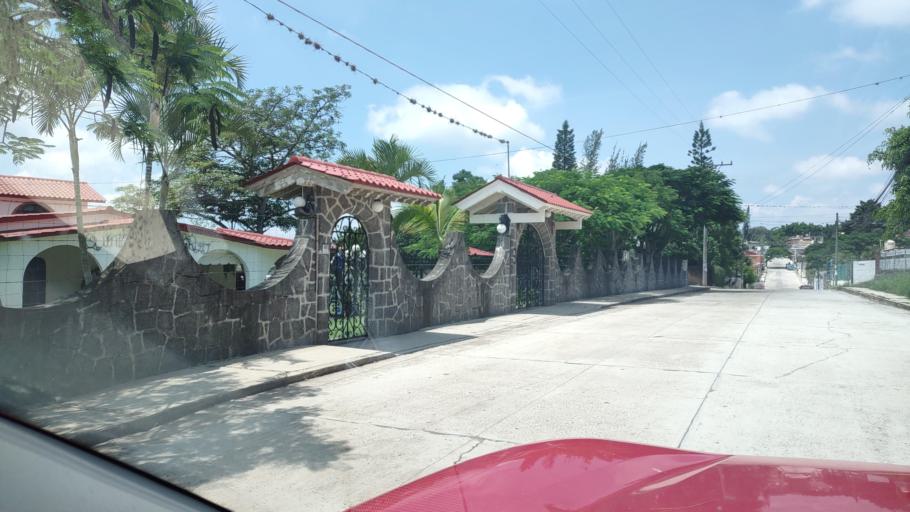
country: MX
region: Veracruz
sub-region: Emiliano Zapata
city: Dos Rios
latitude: 19.4896
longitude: -96.8139
